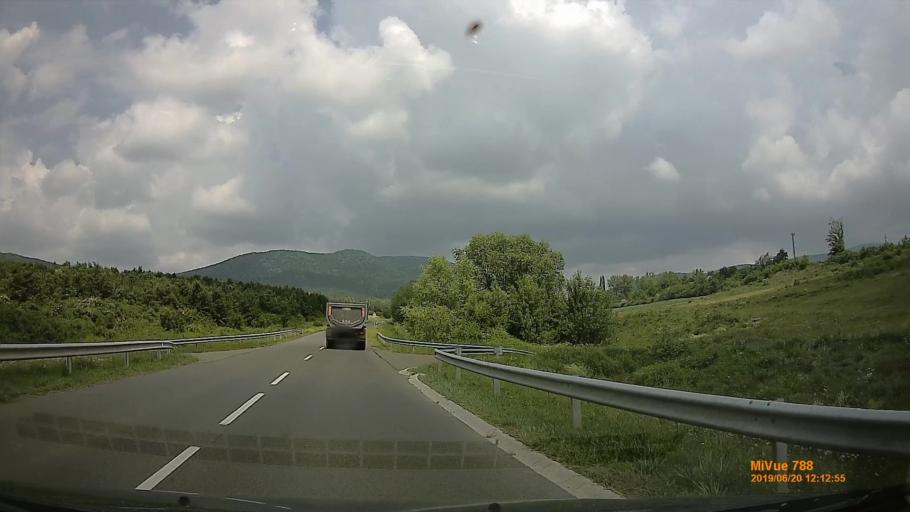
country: HU
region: Baranya
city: Hosszuheteny
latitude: 46.1523
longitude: 18.3436
